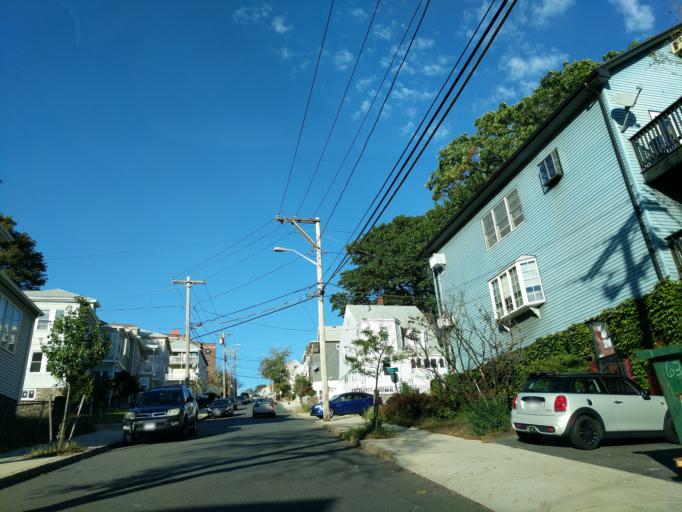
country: US
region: Massachusetts
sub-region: Middlesex County
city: Everett
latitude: 42.4078
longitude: -71.0397
